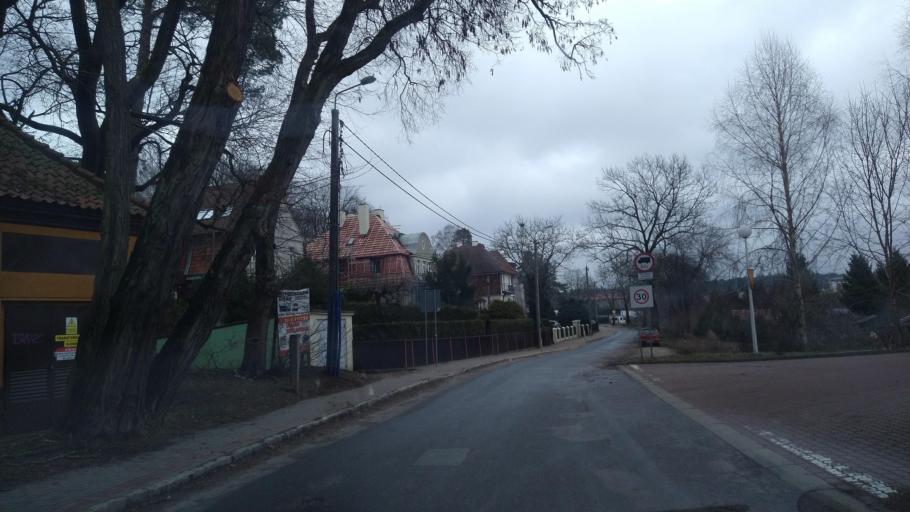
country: PL
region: Warmian-Masurian Voivodeship
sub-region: Powiat olsztynski
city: Olsztyn
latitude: 53.7975
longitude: 20.4830
